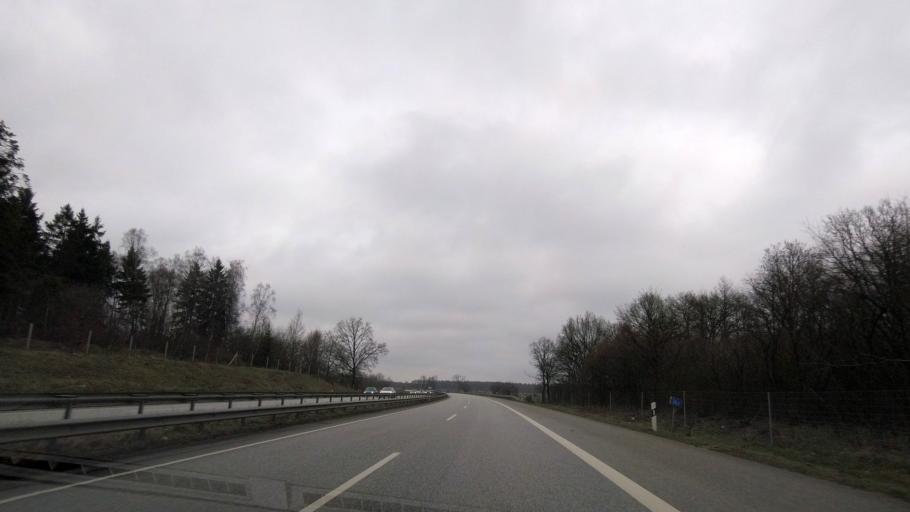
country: DE
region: Schleswig-Holstein
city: Negernbotel
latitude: 53.9983
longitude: 10.2513
